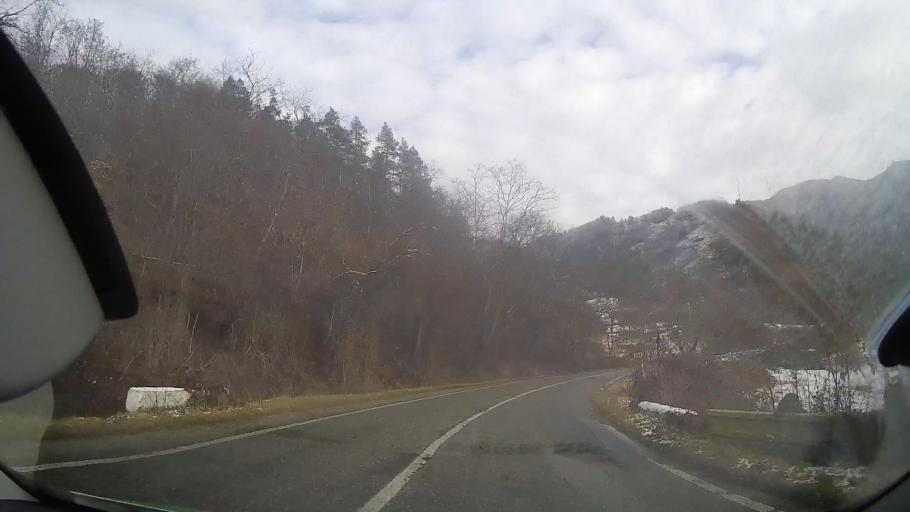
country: RO
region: Alba
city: Salciua de Sus
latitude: 46.4070
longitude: 23.4473
